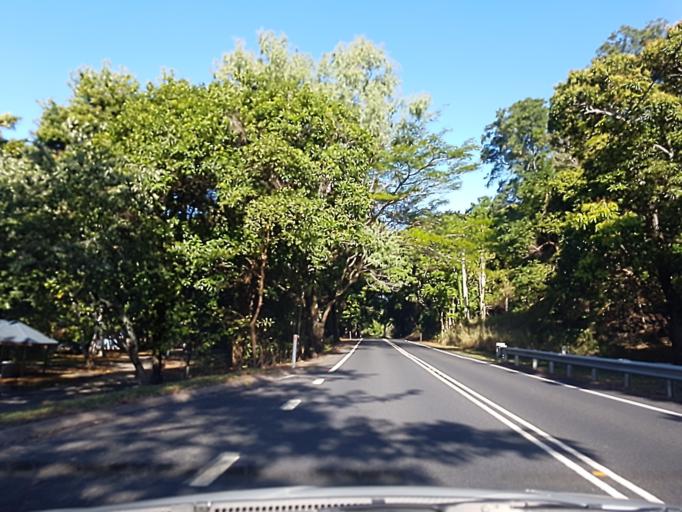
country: AU
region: Queensland
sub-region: Cairns
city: Palm Cove
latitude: -16.7243
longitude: 145.6445
